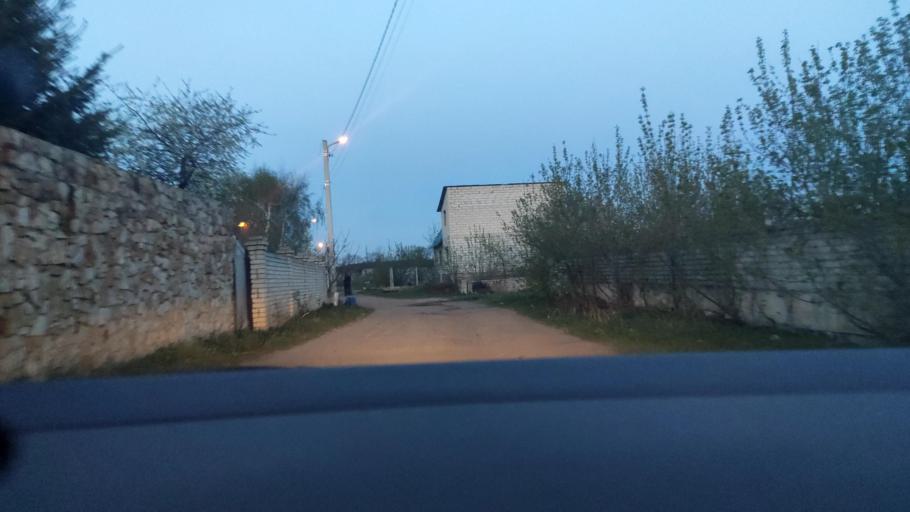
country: RU
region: Voronezj
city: Somovo
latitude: 51.7363
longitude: 39.3224
